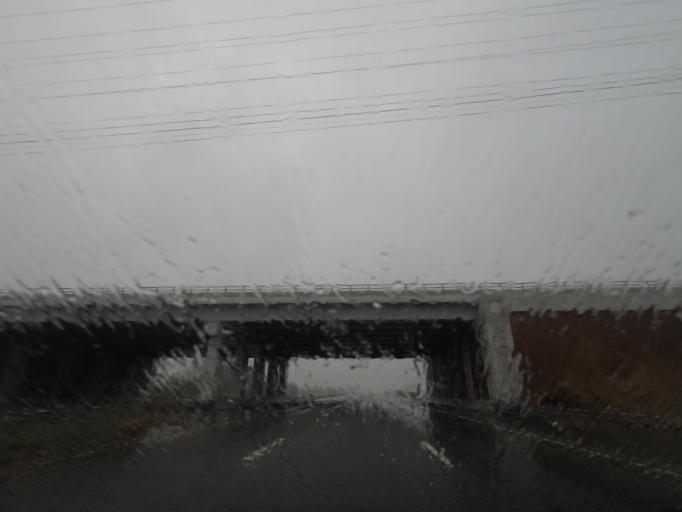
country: US
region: North Carolina
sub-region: Wake County
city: Morrisville
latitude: 35.8770
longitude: -78.8669
